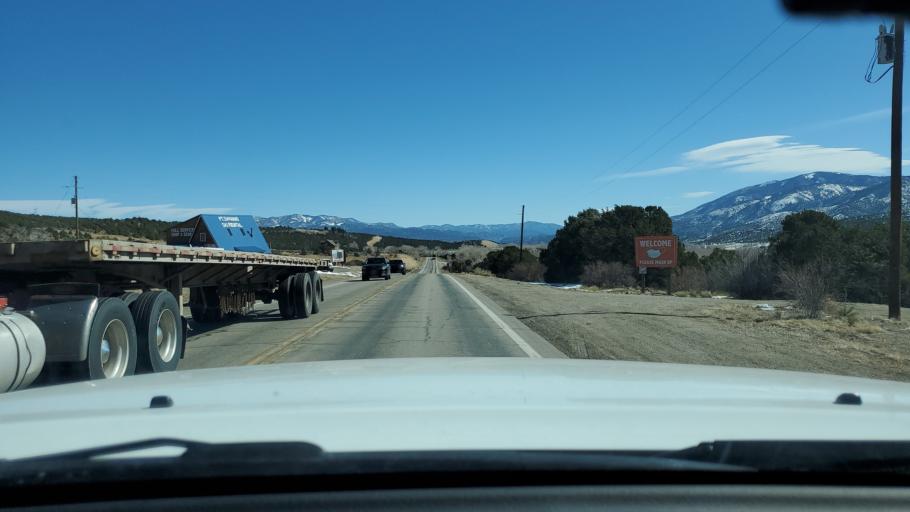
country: US
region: Colorado
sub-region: Chaffee County
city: Salida
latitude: 38.5360
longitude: -106.1753
